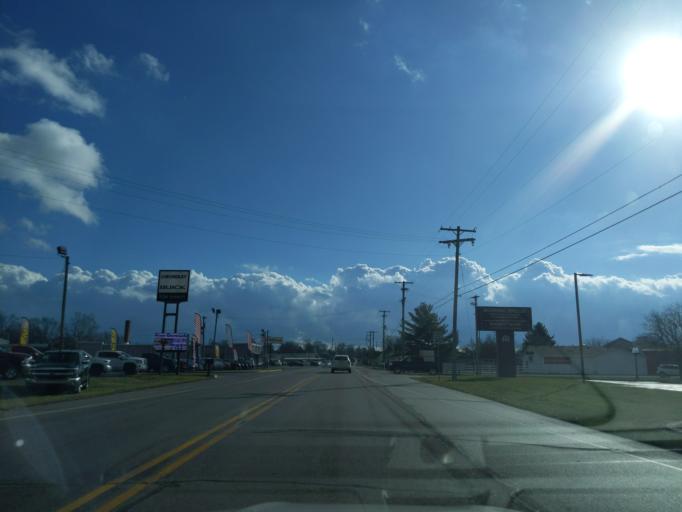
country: US
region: Indiana
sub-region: Decatur County
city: Greensburg
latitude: 39.3464
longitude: -85.4955
